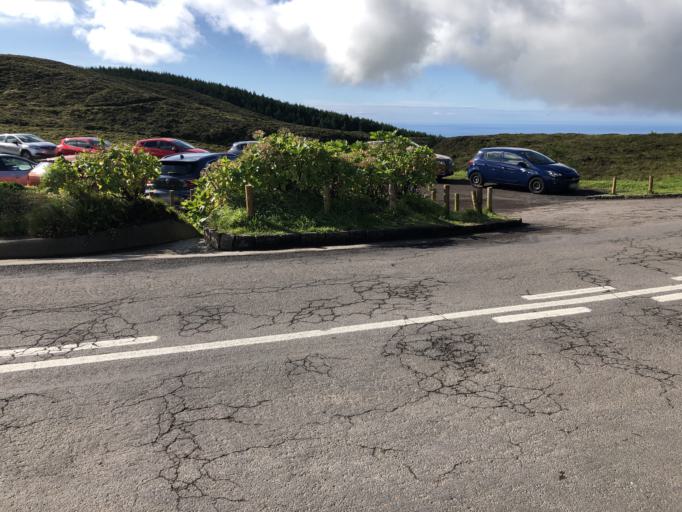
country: PT
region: Azores
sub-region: Ponta Delgada
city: Arrifes
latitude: 37.8350
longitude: -25.7586
